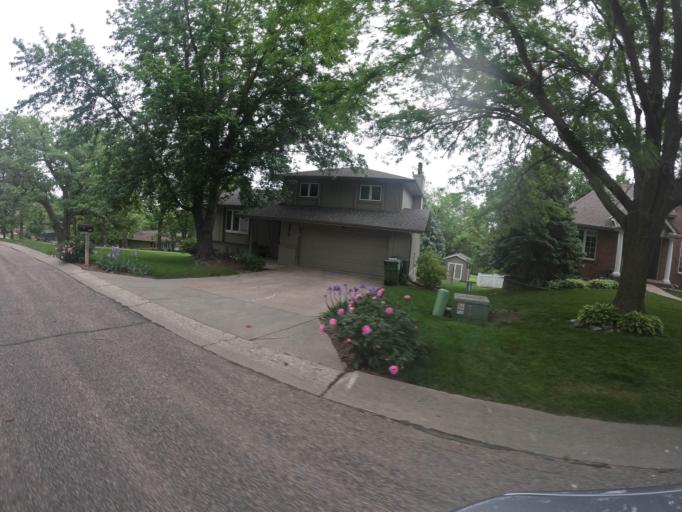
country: US
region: Nebraska
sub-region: Sarpy County
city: Offutt Air Force Base
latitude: 41.0477
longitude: -95.9683
